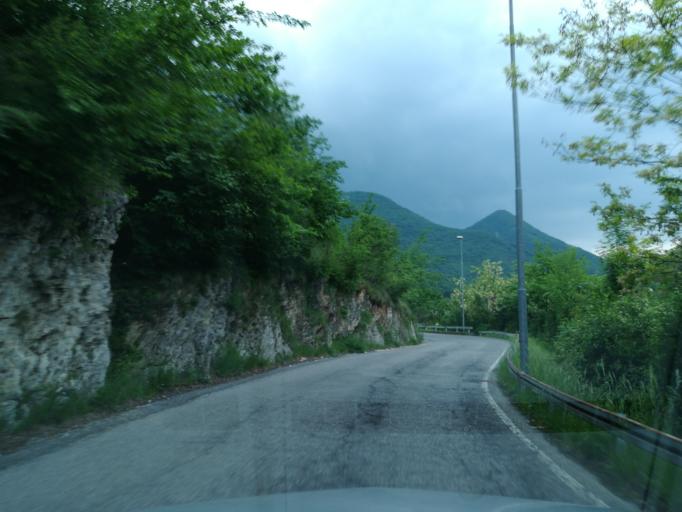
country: IT
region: Lombardy
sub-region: Provincia di Bergamo
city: Camoneone
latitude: 45.7918
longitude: 9.5672
